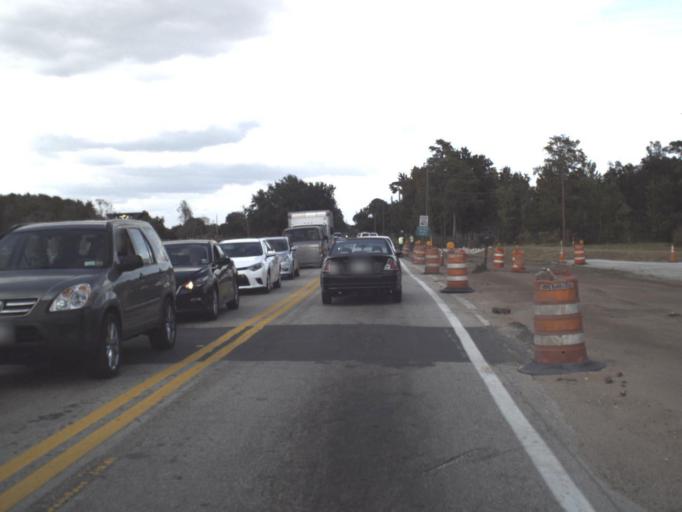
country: US
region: Florida
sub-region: Osceola County
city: Buenaventura Lakes
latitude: 28.3486
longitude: -81.3095
